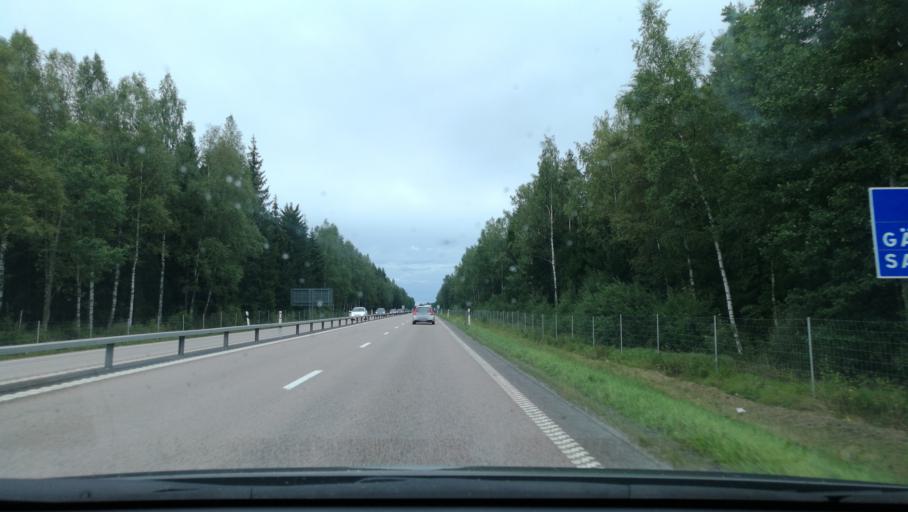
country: SE
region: Vaestmanland
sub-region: Vasteras
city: Hokasen
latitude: 59.6583
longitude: 16.5784
